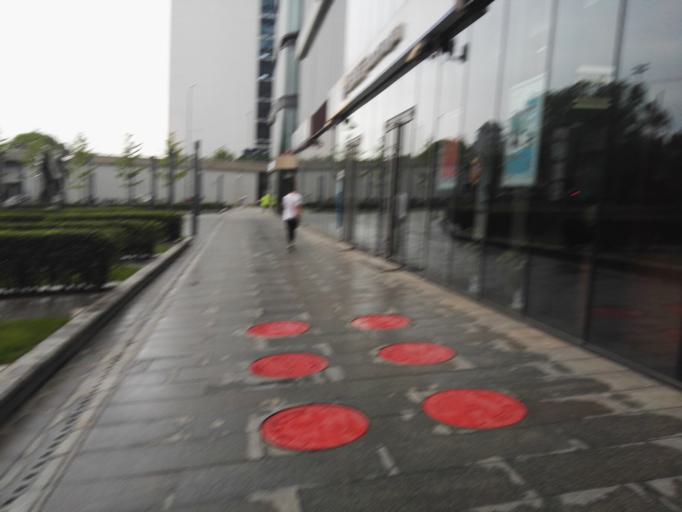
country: CN
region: Beijing
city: Haidian
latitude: 39.9833
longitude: 116.3011
